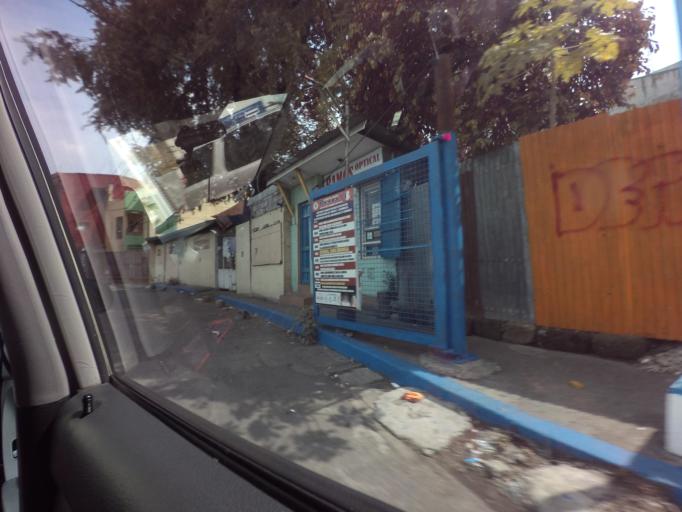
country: PH
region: Metro Manila
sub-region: San Juan
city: San Juan
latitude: 14.6024
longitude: 121.0145
